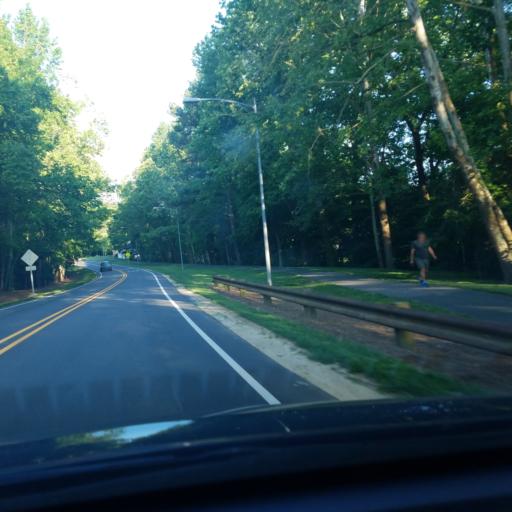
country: US
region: North Carolina
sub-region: Durham County
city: Durham
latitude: 35.9226
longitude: -78.9525
